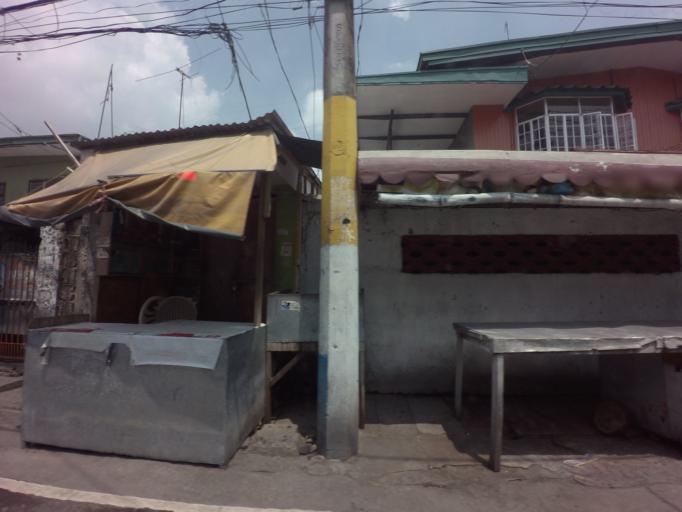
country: PH
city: Sambayanihan People's Village
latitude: 14.4438
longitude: 121.0505
